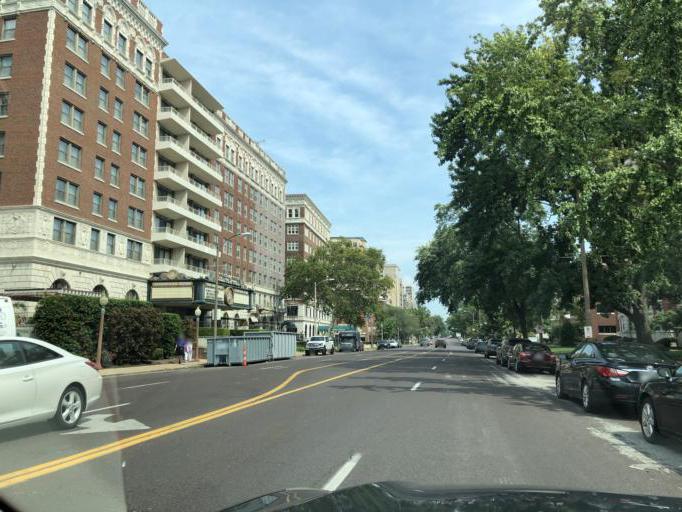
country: US
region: Missouri
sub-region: Saint Louis County
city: Hillsdale
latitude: 38.6437
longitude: -90.2642
